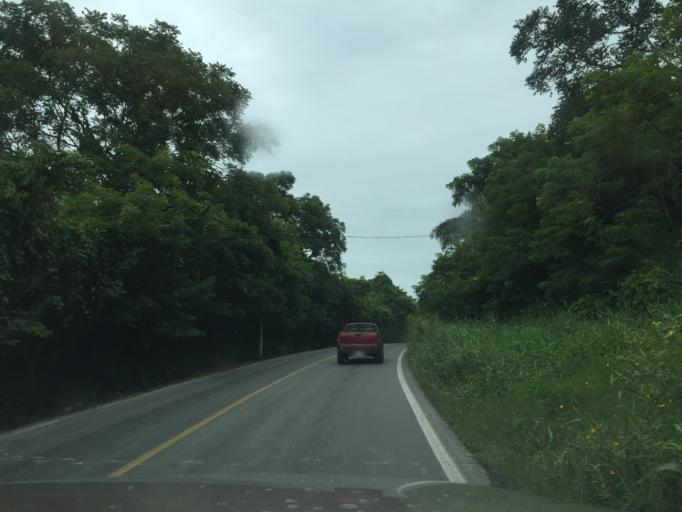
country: MX
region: Veracruz
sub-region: Papantla
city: El Chote
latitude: 20.4383
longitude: -97.3891
